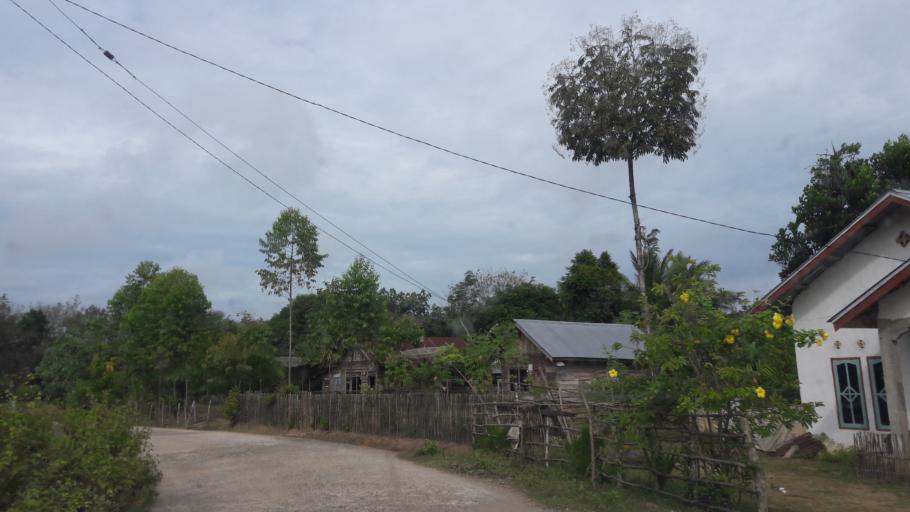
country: ID
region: South Sumatra
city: Gunungmegang Dalam
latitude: -3.2978
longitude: 103.6750
